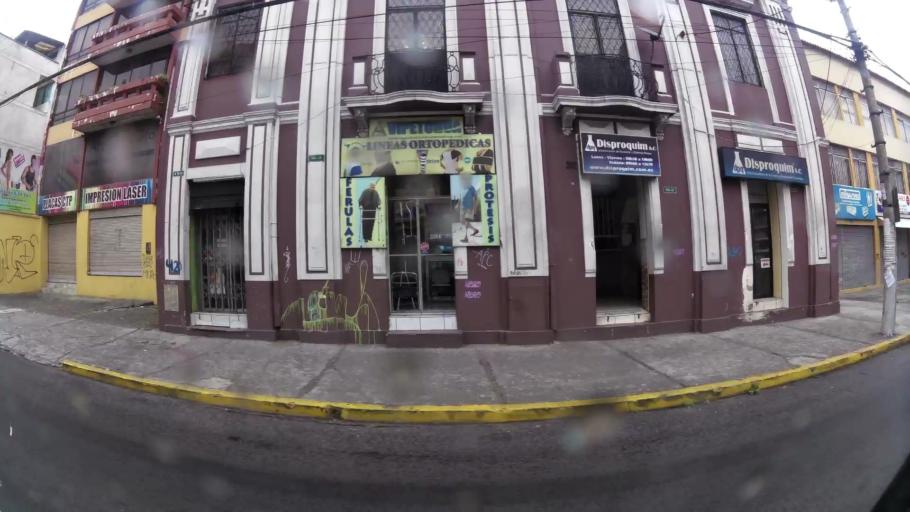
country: EC
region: Pichincha
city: Quito
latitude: -0.2093
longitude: -78.5036
